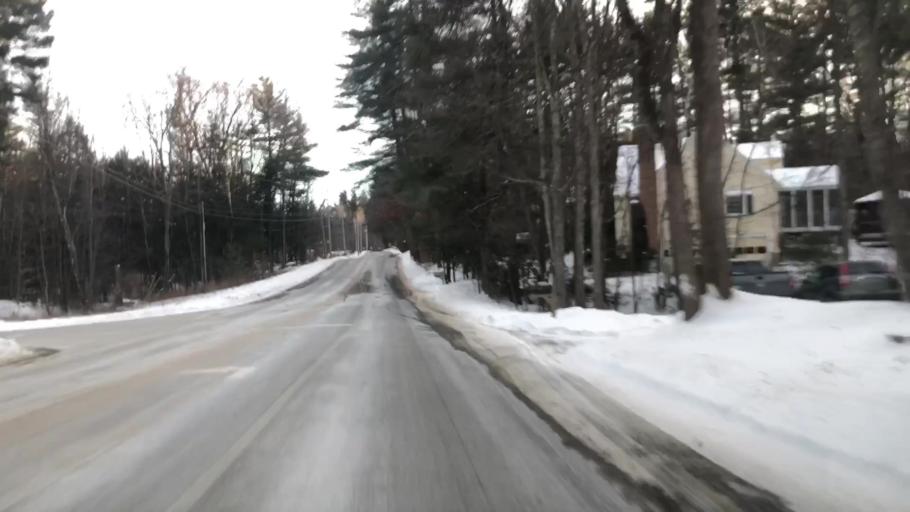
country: US
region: New Hampshire
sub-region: Hillsborough County
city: Wilton
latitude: 42.8236
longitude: -71.6958
